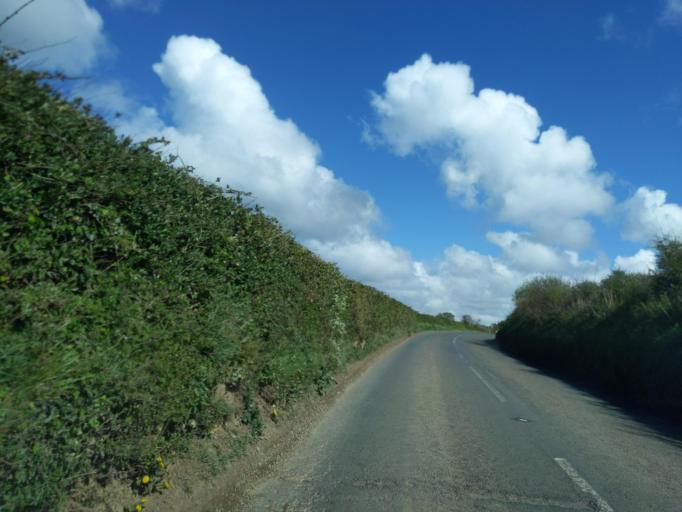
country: GB
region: England
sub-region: Cornwall
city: Wadebridge
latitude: 50.5739
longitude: -4.8418
